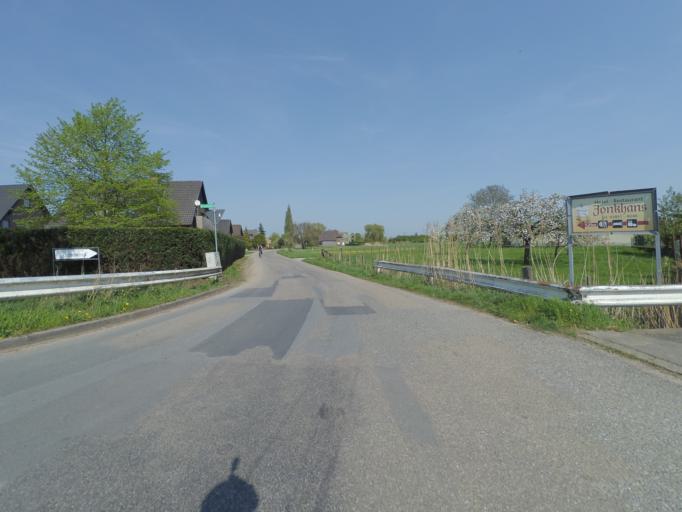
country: DE
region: North Rhine-Westphalia
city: Rees
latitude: 51.8105
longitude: 6.3932
